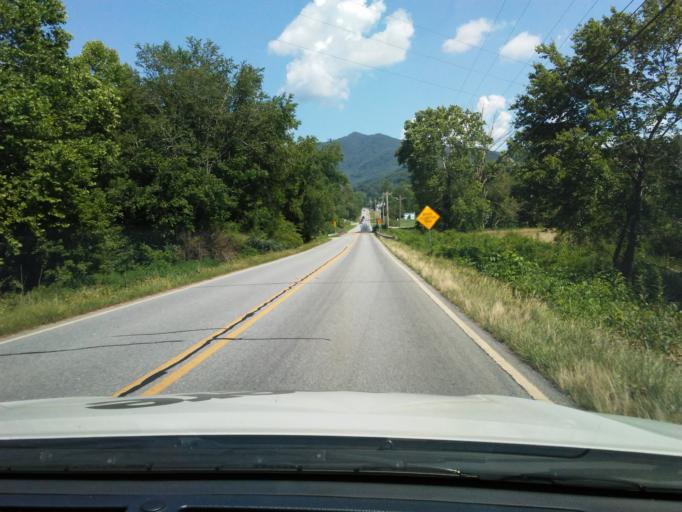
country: US
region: Georgia
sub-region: Towns County
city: Hiawassee
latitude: 34.9404
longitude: -83.8575
